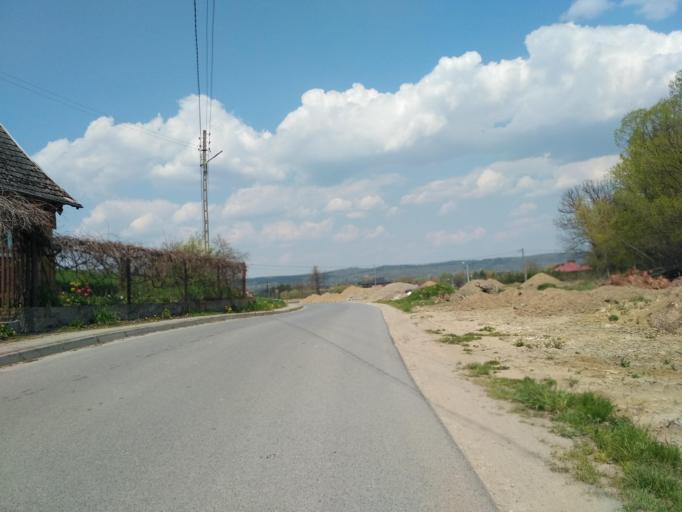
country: PL
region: Subcarpathian Voivodeship
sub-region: Powiat jasielski
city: Jaslo
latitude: 49.7304
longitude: 21.5106
